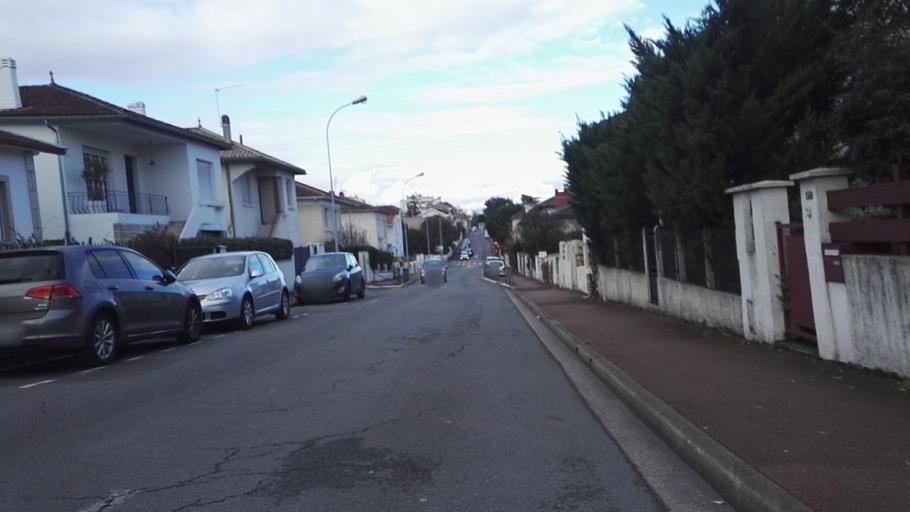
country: FR
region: Aquitaine
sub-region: Departement de la Gironde
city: Talence
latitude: 44.8074
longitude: -0.5862
